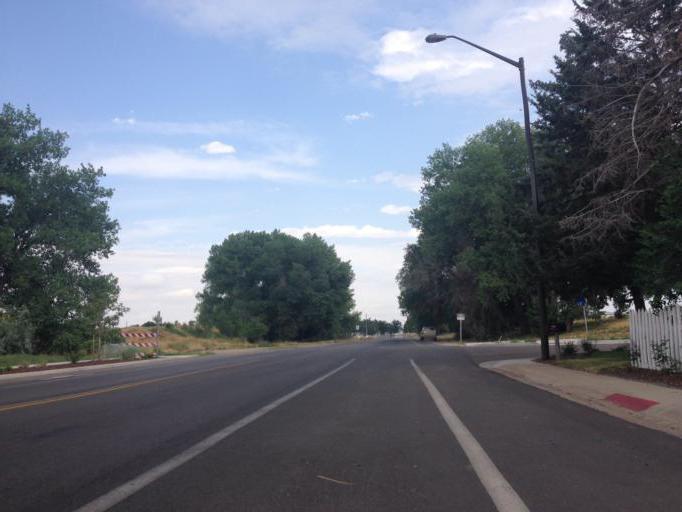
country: US
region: Colorado
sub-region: Larimer County
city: Fort Collins
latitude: 40.5924
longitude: -105.0653
